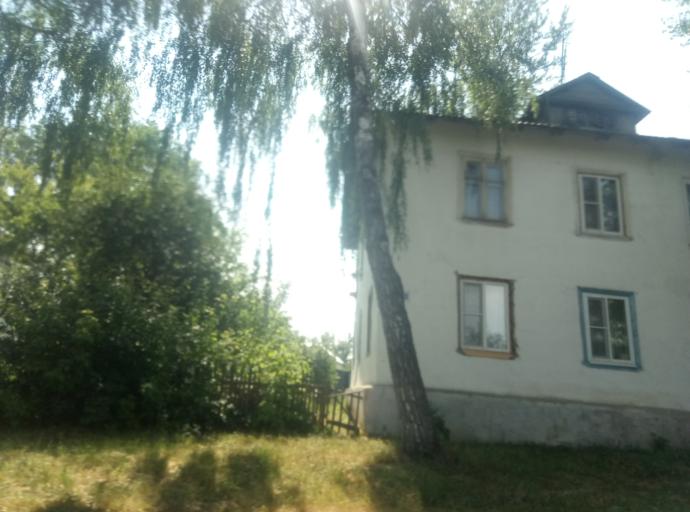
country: RU
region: Tula
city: Kireyevsk
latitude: 53.9317
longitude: 37.9357
